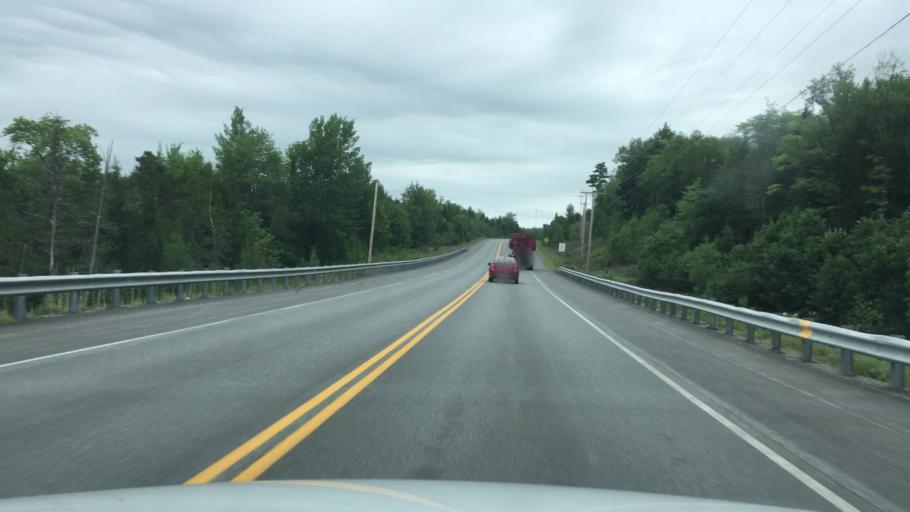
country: US
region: Maine
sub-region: Hancock County
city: Franklin
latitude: 44.8421
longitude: -68.3439
